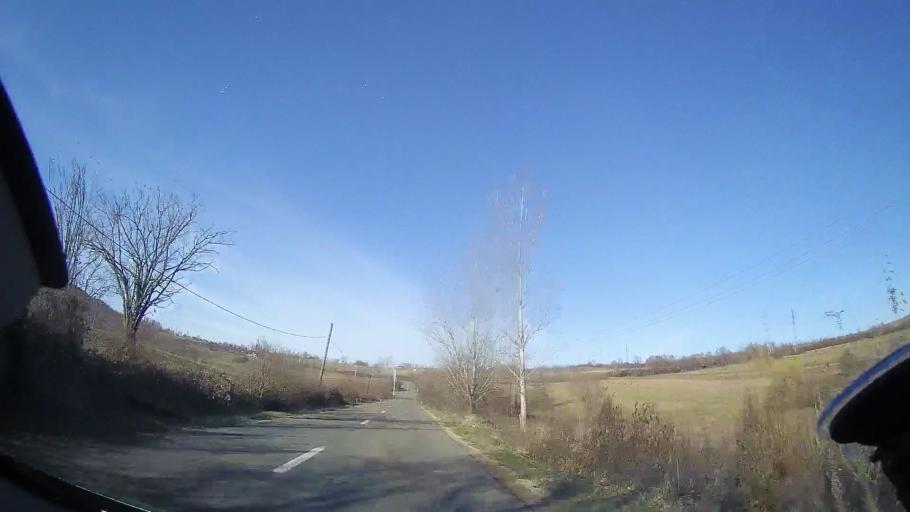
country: RO
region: Bihor
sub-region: Comuna Suncuius
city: Balnaca
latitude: 46.9684
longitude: 22.5492
